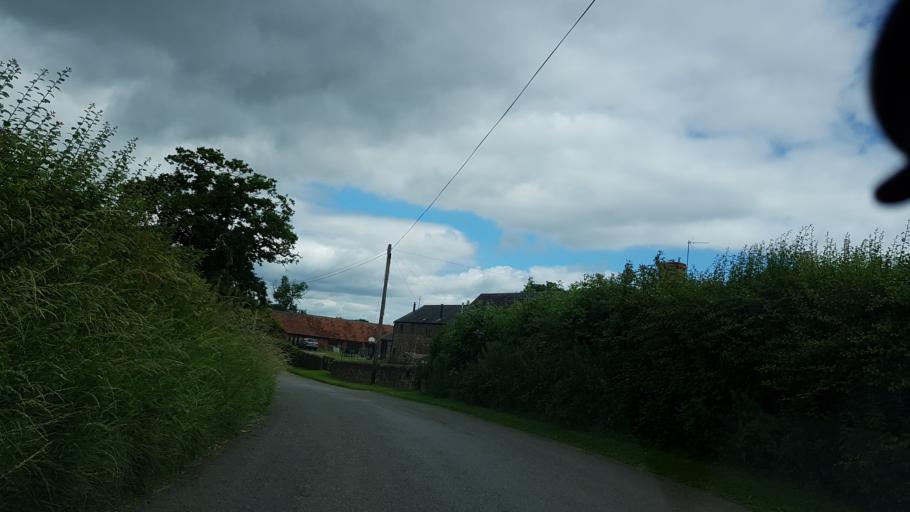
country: GB
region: Wales
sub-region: Monmouthshire
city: Llanarth
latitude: 51.7776
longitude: -2.8329
